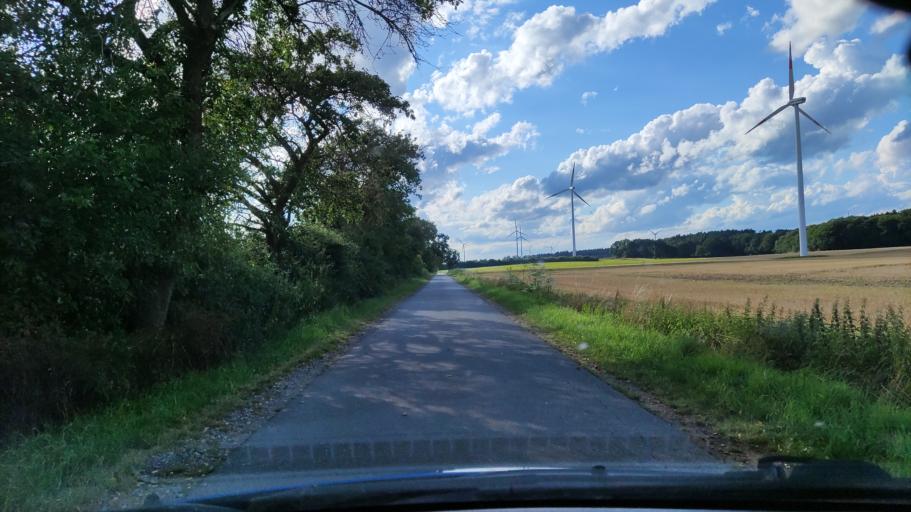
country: DE
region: Lower Saxony
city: Nahrendorf
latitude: 53.1756
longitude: 10.8063
